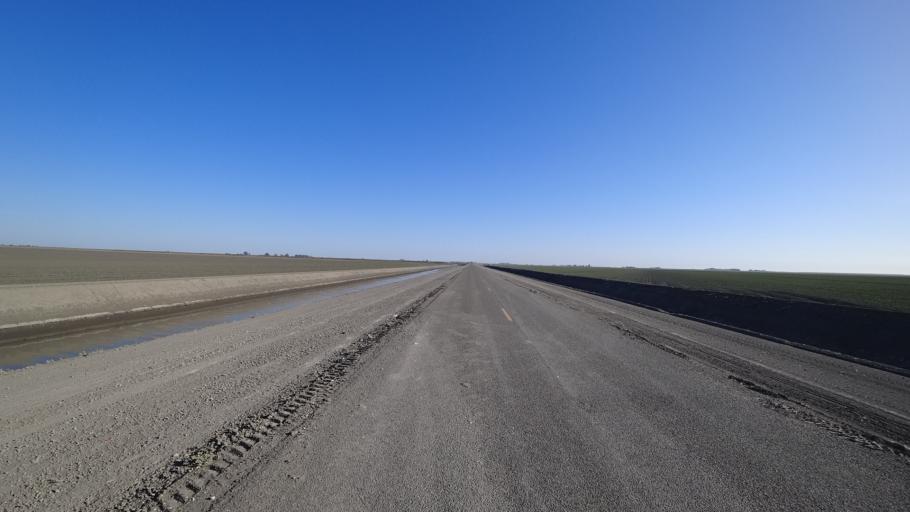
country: US
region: California
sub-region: Kings County
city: Stratford
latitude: 36.1325
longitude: -119.7981
